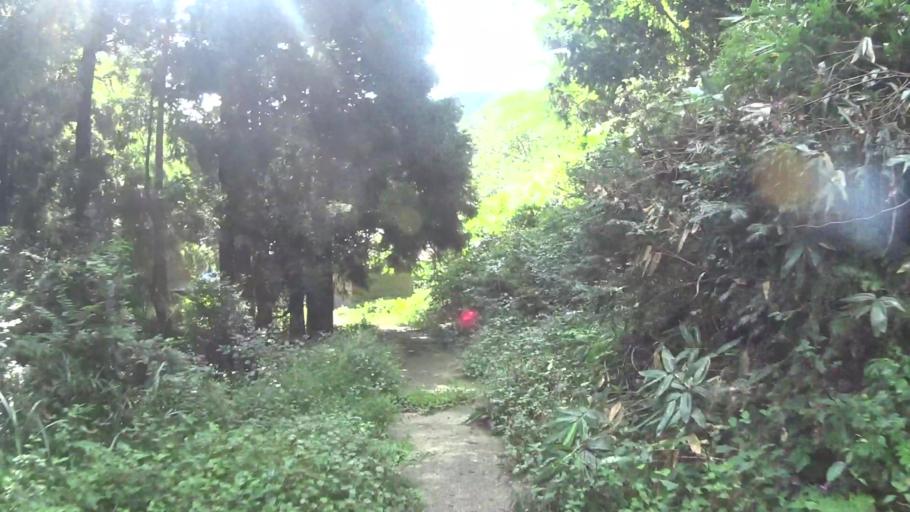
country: JP
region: Kyoto
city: Miyazu
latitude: 35.6125
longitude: 135.1954
